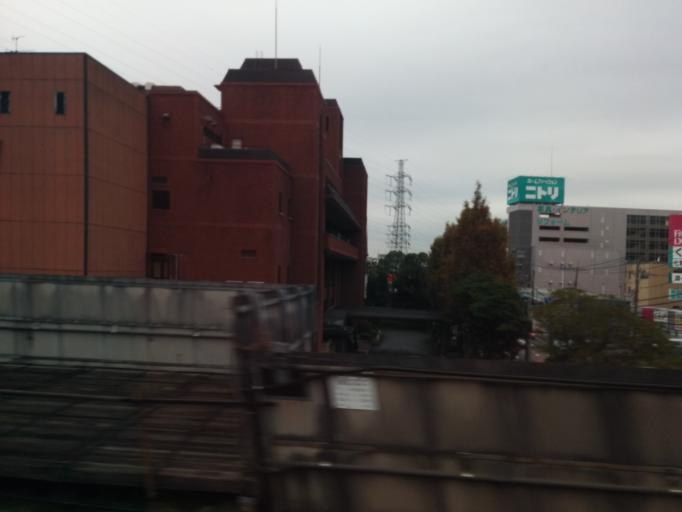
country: JP
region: Kanagawa
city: Yokohama
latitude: 35.5012
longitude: 139.6096
